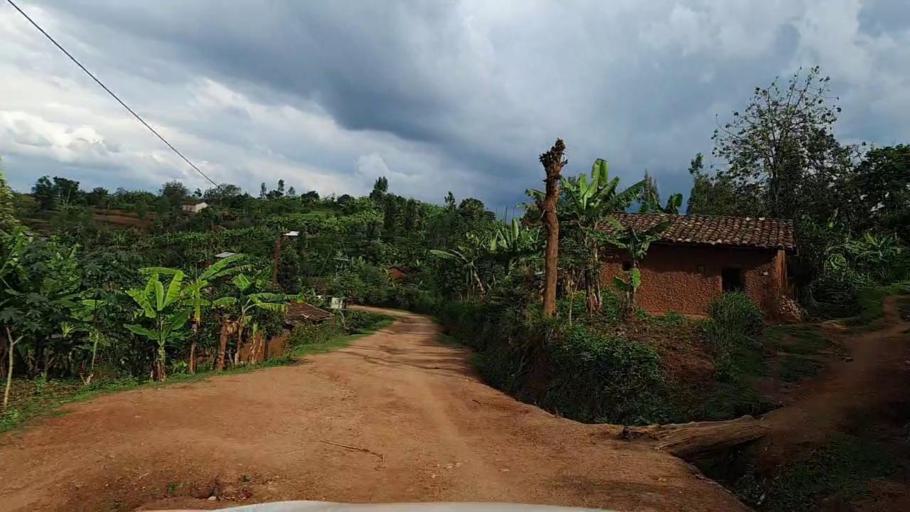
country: RW
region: Southern Province
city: Gikongoro
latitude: -2.4241
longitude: 29.6446
